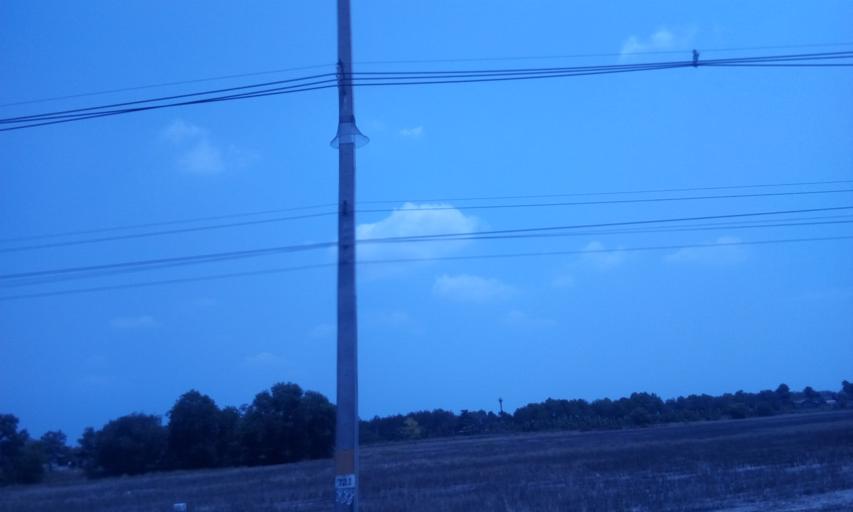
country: TH
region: Chachoengsao
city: Bang Nam Priao
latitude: 13.8385
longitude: 101.0538
